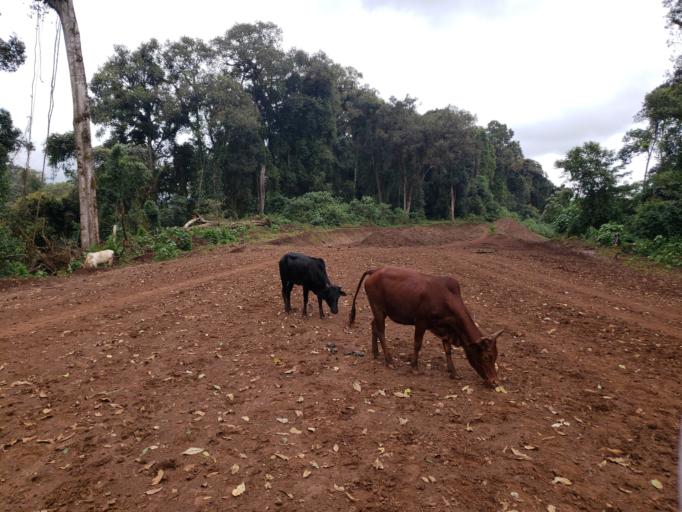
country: ET
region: Oromiya
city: Dodola
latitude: 6.5853
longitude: 39.4148
